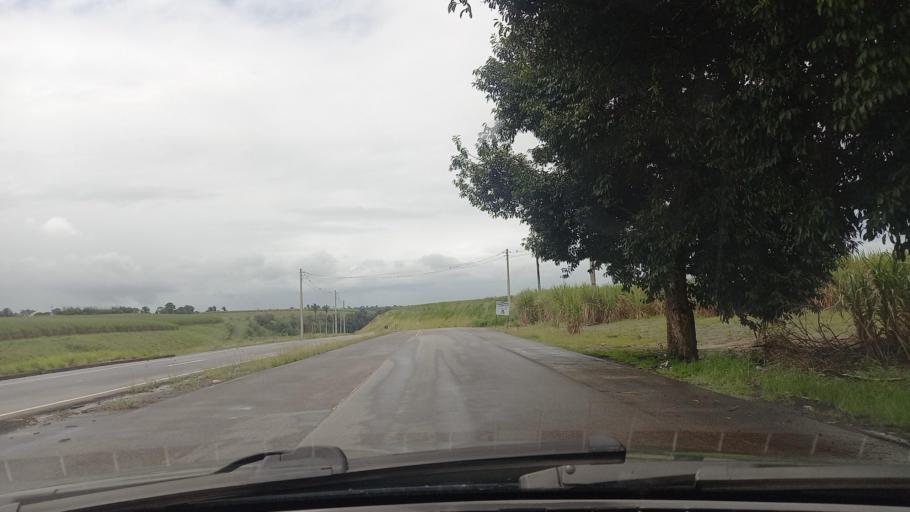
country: BR
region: Alagoas
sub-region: Campo Alegre
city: Campo Alegre
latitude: -9.8229
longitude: -36.2333
